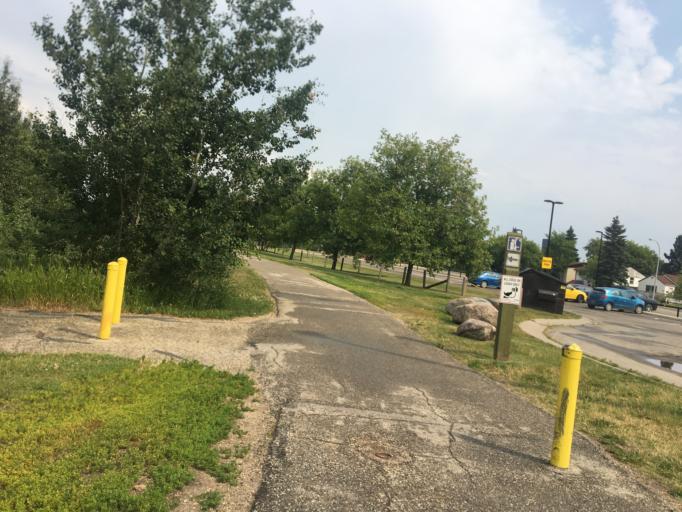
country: CA
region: Alberta
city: Grande Prairie
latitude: 55.1749
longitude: -118.8111
